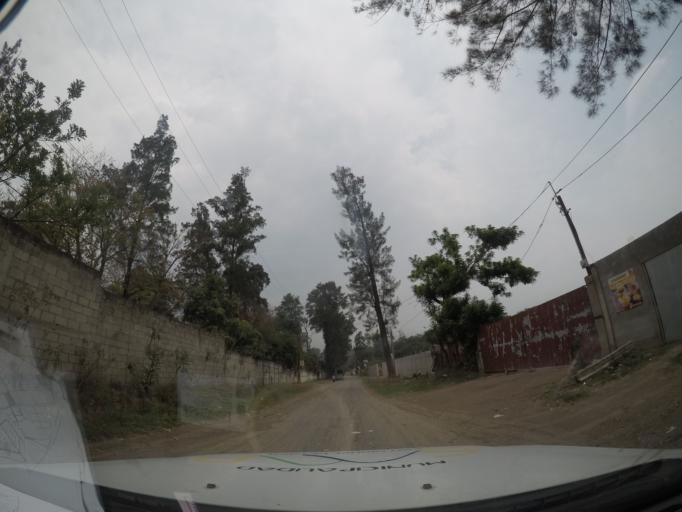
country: GT
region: Guatemala
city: Petapa
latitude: 14.5031
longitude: -90.5492
